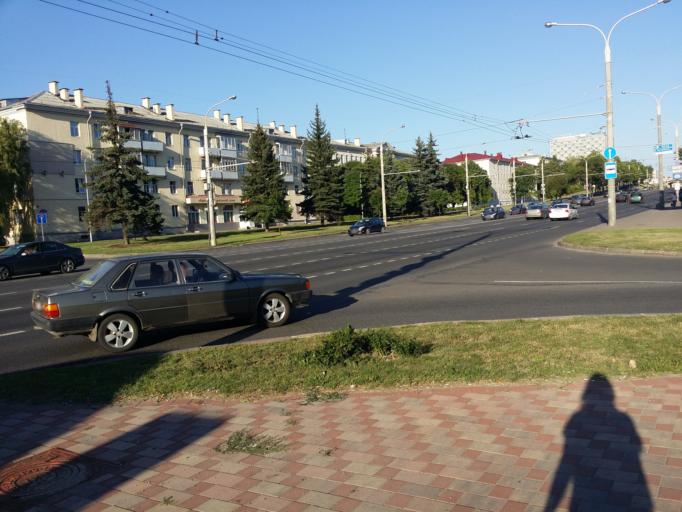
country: BY
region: Minsk
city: Minsk
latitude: 53.8766
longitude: 27.6192
